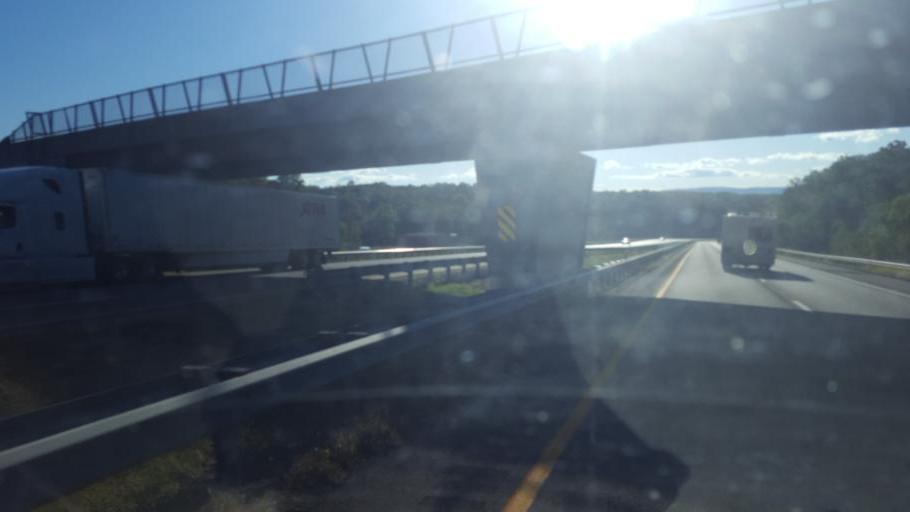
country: US
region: Maryland
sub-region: Allegany County
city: Cumberland
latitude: 39.6948
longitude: -78.5103
